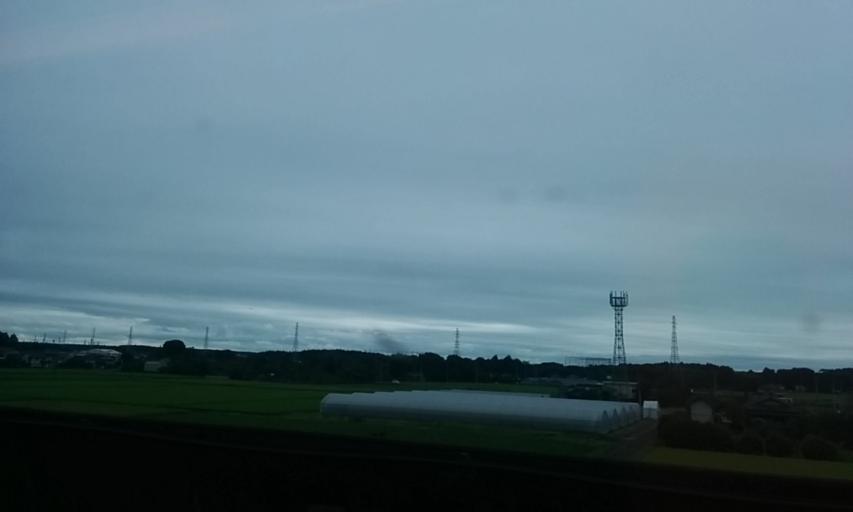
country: JP
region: Tochigi
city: Utsunomiya-shi
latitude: 36.5990
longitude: 139.9058
